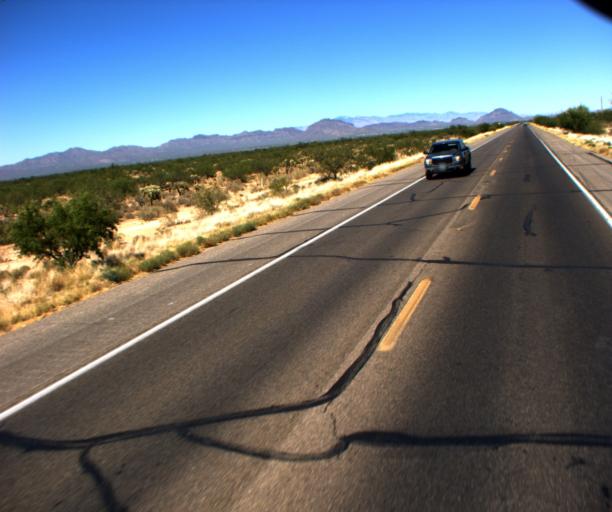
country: US
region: Arizona
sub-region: Pima County
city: Three Points
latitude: 32.1078
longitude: -111.2355
